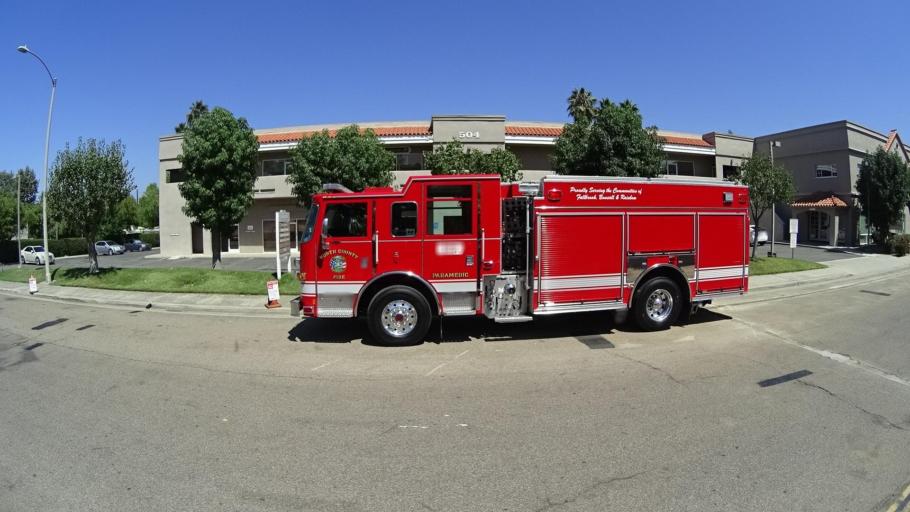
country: US
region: California
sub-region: San Diego County
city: Fallbrook
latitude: 33.3820
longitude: -117.2471
